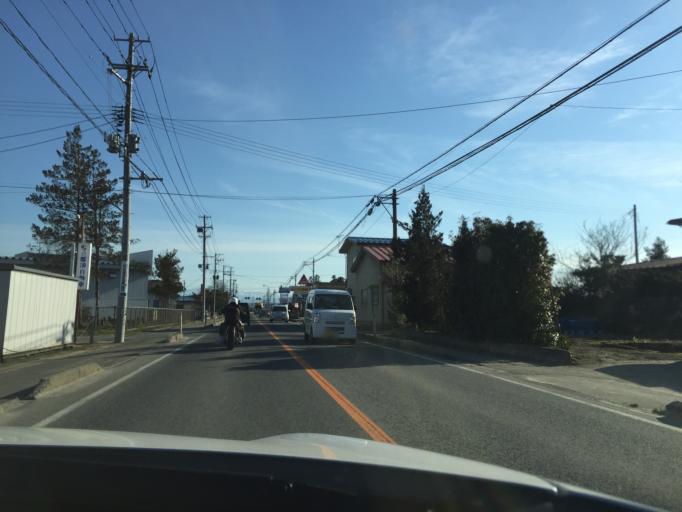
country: JP
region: Yamagata
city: Nagai
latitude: 38.0831
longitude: 140.0402
